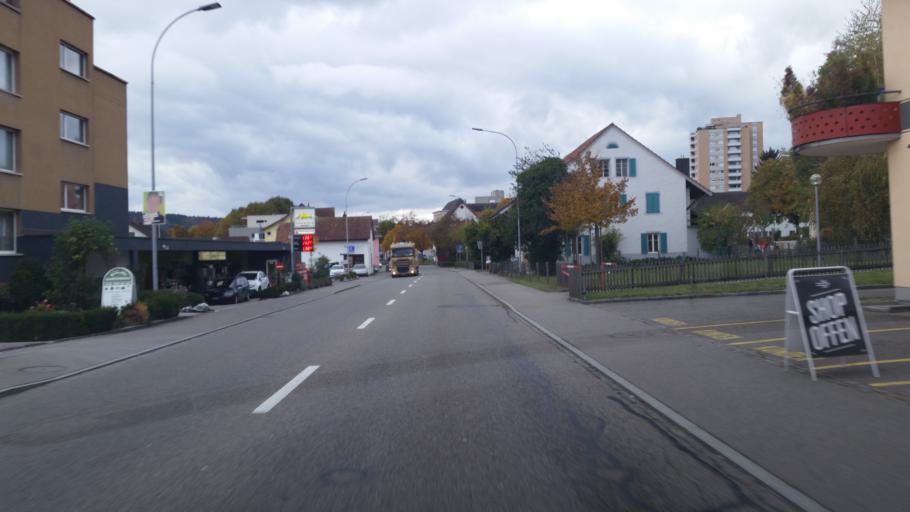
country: CH
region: Aargau
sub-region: Bezirk Baden
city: Obersiggenthal
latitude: 47.4866
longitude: 8.2958
